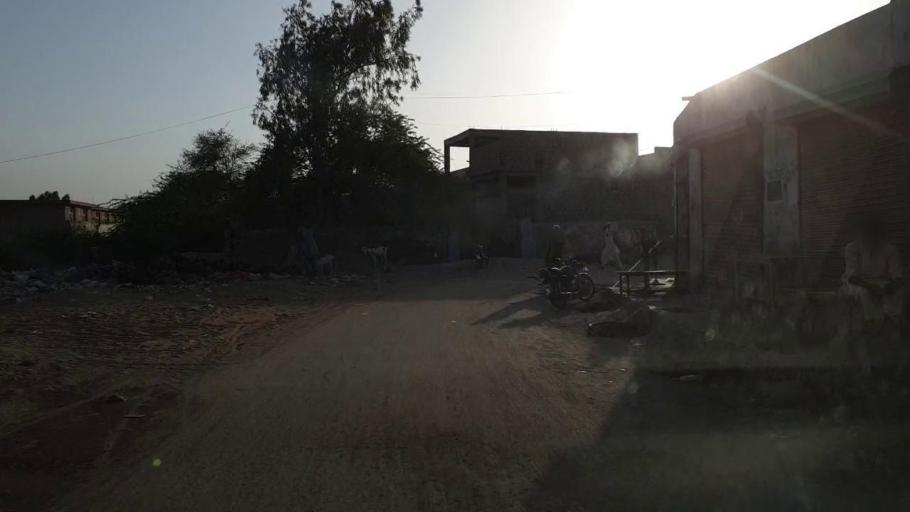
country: PK
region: Sindh
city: Jam Sahib
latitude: 26.2940
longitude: 68.6297
